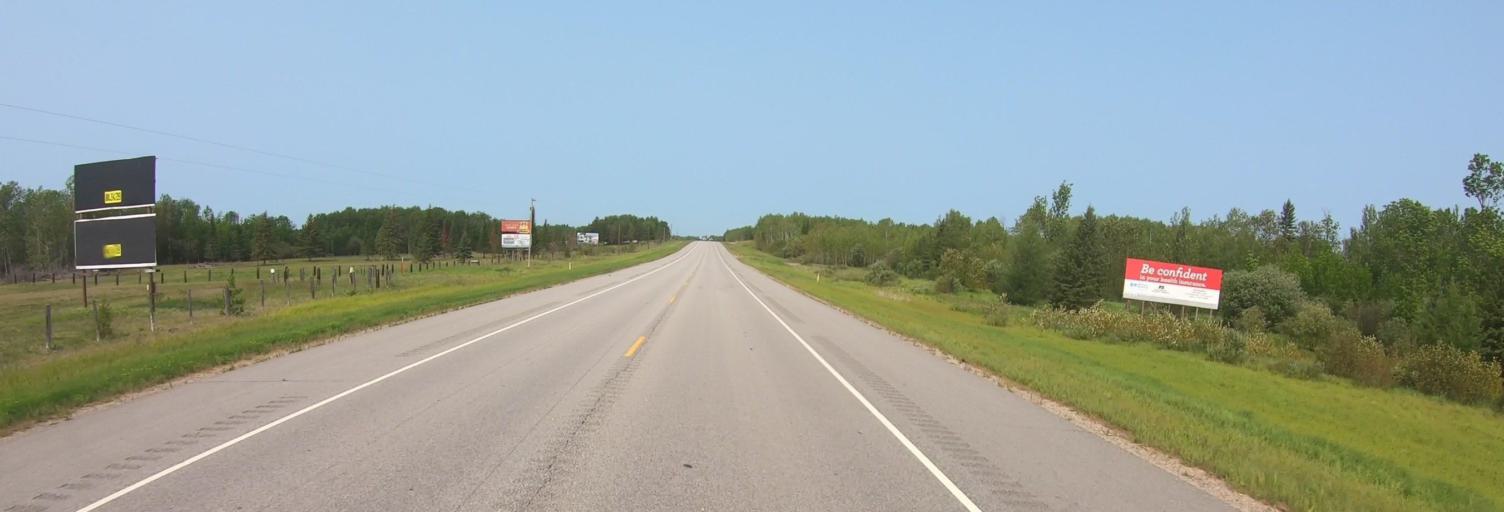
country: CA
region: Ontario
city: Fort Frances
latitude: 48.4148
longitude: -93.2097
